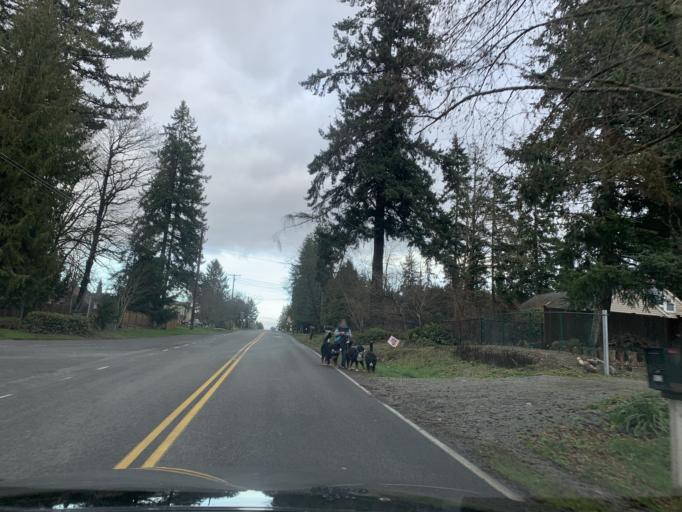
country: US
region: Washington
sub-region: Pierce County
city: Edgewood
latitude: 47.2427
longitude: -122.3009
